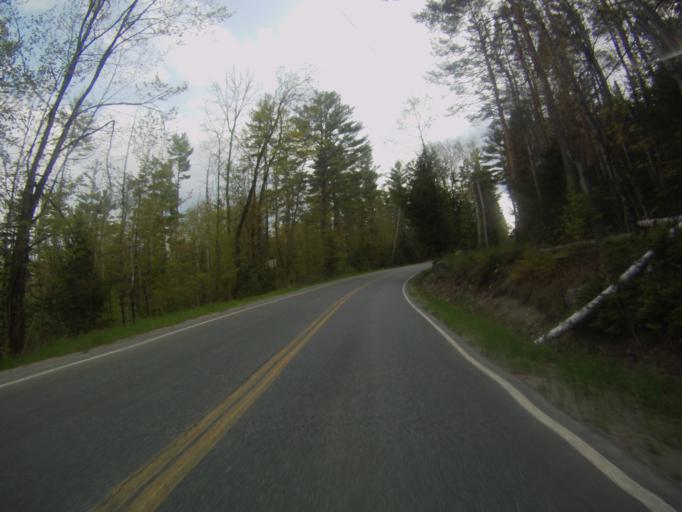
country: US
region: New York
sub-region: Warren County
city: Warrensburg
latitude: 43.8390
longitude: -73.8743
